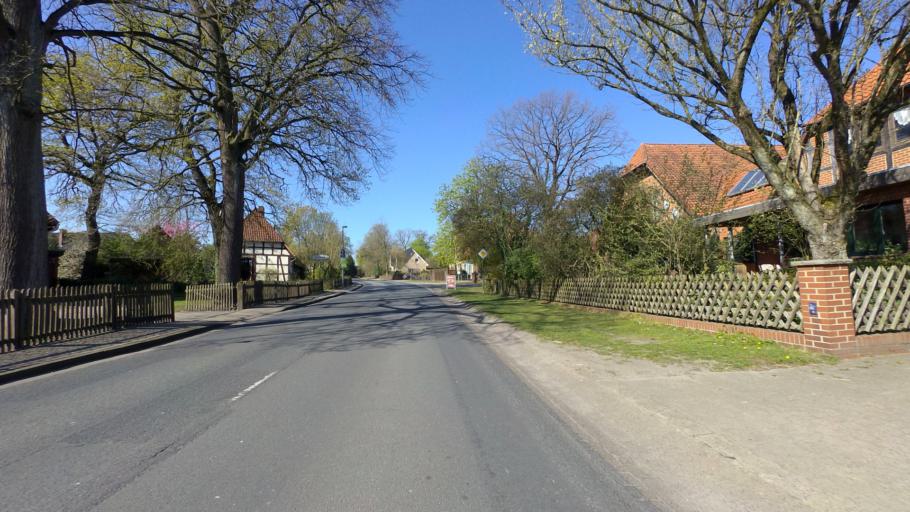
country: DE
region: Lower Saxony
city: Stockse
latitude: 52.6400
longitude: 9.3400
